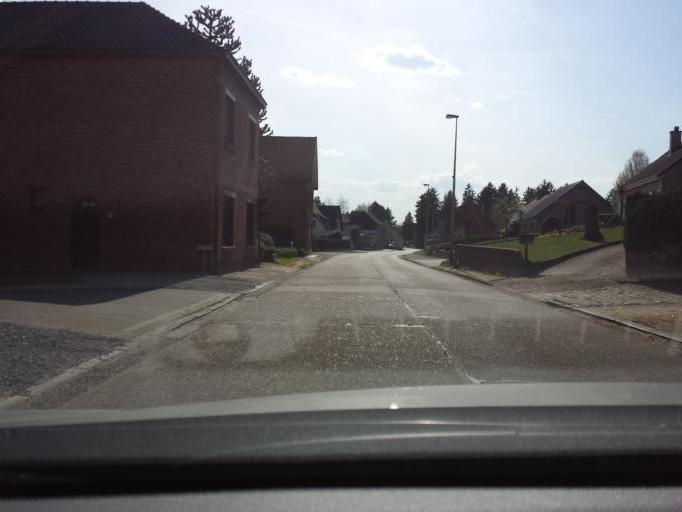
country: BE
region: Flanders
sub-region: Provincie Limburg
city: Lummen
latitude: 50.9982
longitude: 5.1407
